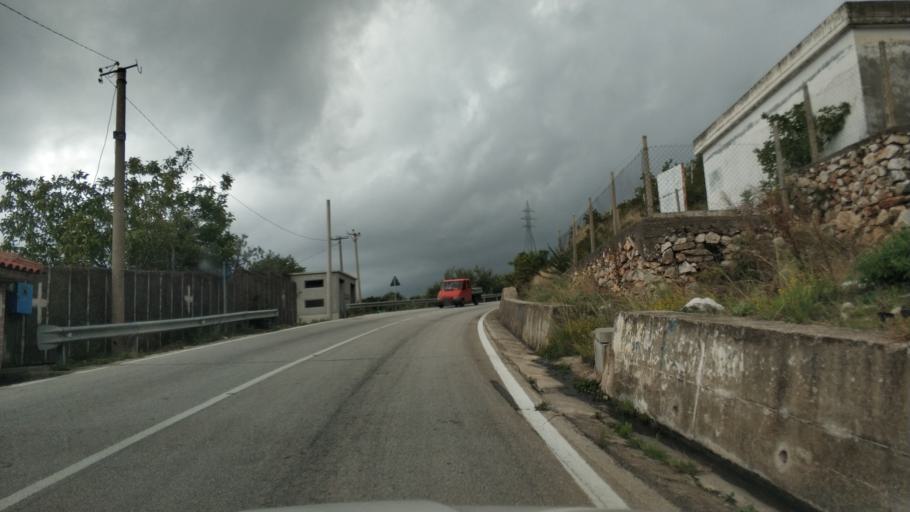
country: AL
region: Vlore
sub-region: Rrethi i Vlores
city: Vranisht
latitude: 40.1580
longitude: 19.6304
